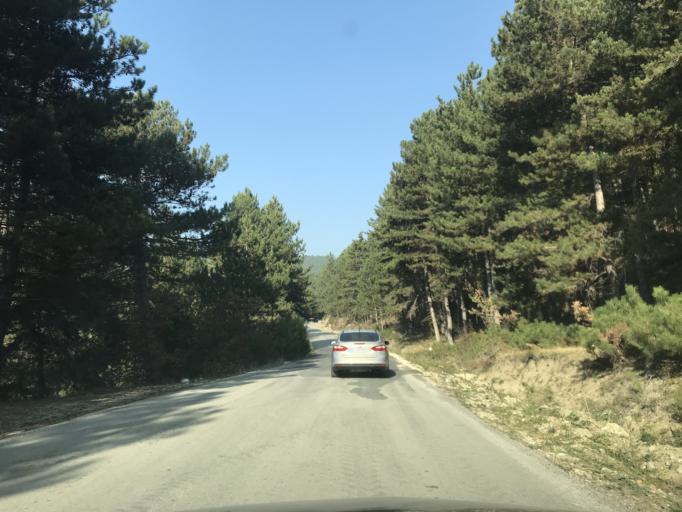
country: TR
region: Bolu
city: Bolu
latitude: 40.7830
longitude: 31.6328
